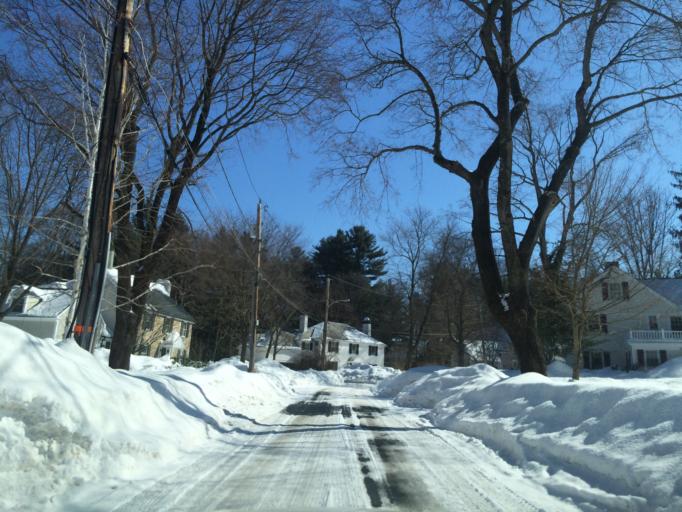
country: US
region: Massachusetts
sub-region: Norfolk County
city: Wellesley
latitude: 42.3011
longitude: -71.2722
